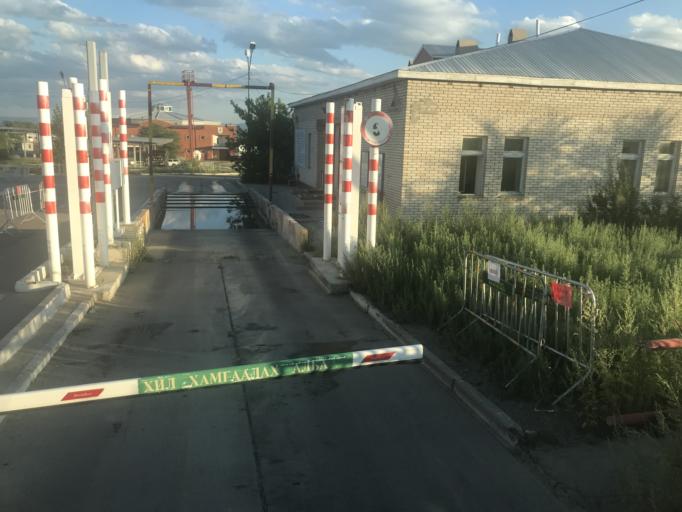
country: MN
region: Selenge
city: Altanbulag
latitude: 50.3233
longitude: 106.4893
